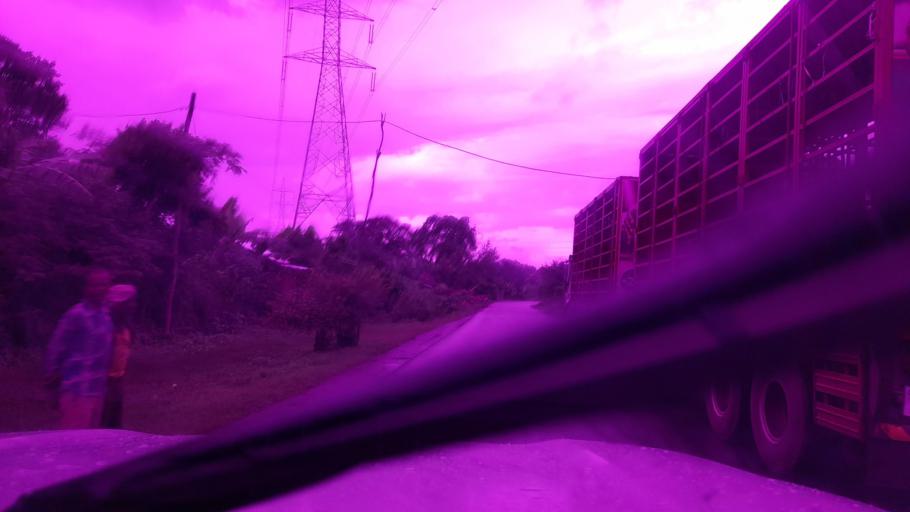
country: ET
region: Oromiya
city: Jima
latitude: 7.7083
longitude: 37.0634
